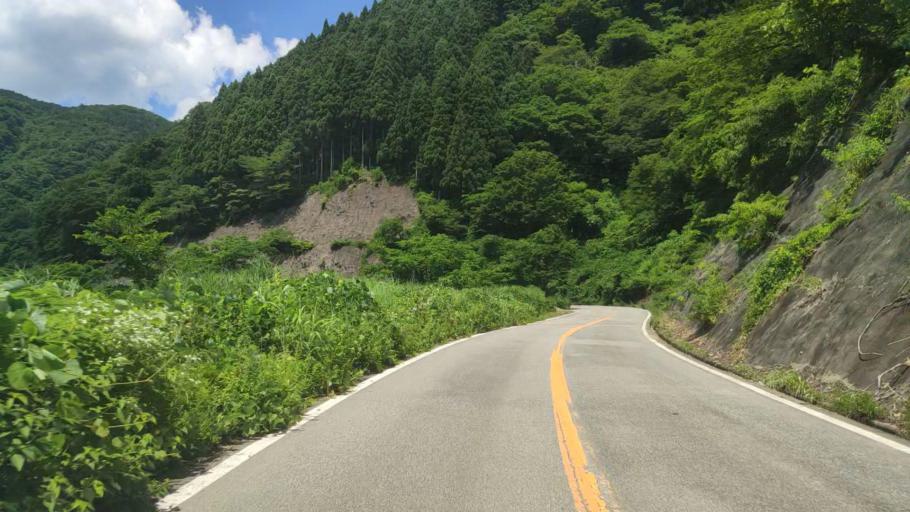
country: JP
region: Fukui
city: Ono
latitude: 35.9167
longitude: 136.5329
